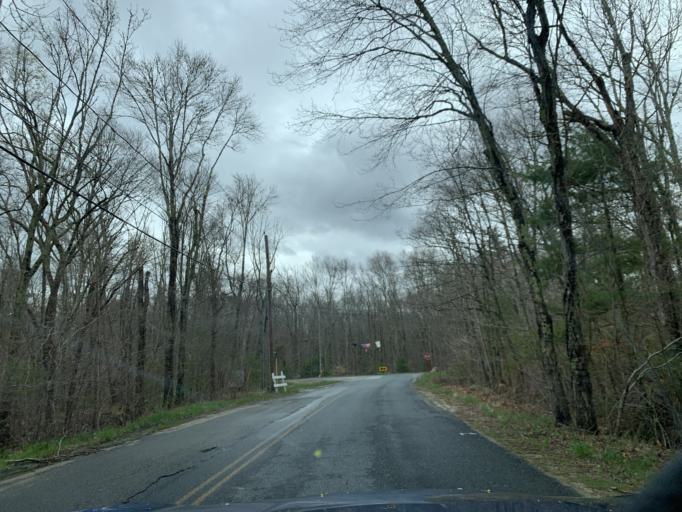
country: US
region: Massachusetts
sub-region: Bristol County
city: Rehoboth
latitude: 41.8762
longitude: -71.2096
